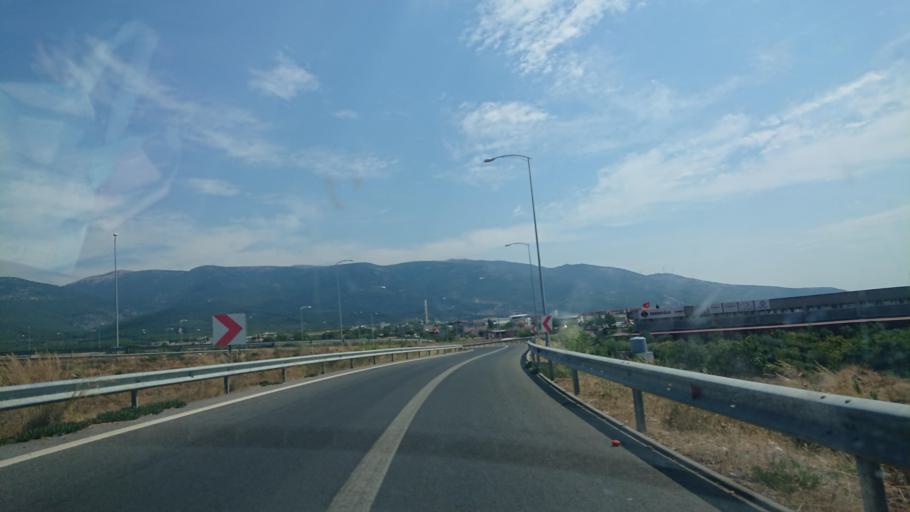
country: TR
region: Izmir
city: Kemalpasa
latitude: 38.4550
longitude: 27.4314
